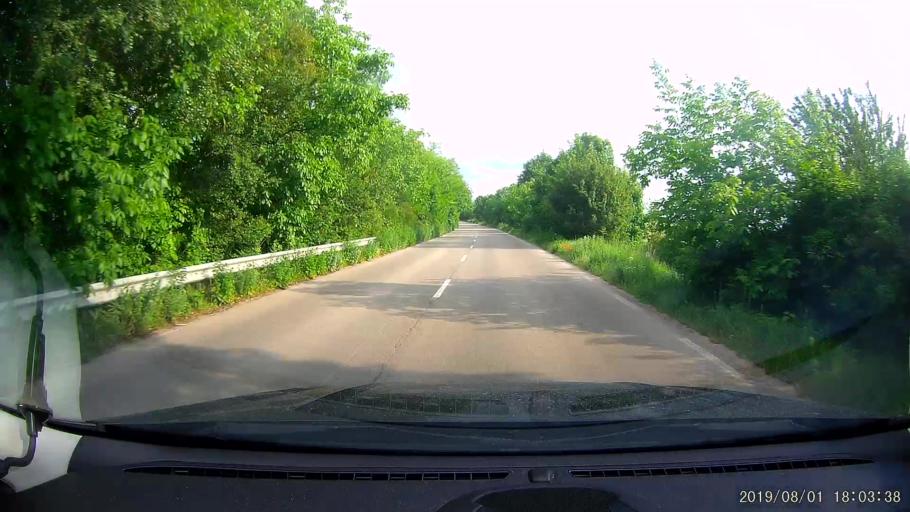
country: BG
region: Silistra
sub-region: Obshtina Alfatar
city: Alfatar
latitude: 43.9232
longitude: 27.2890
